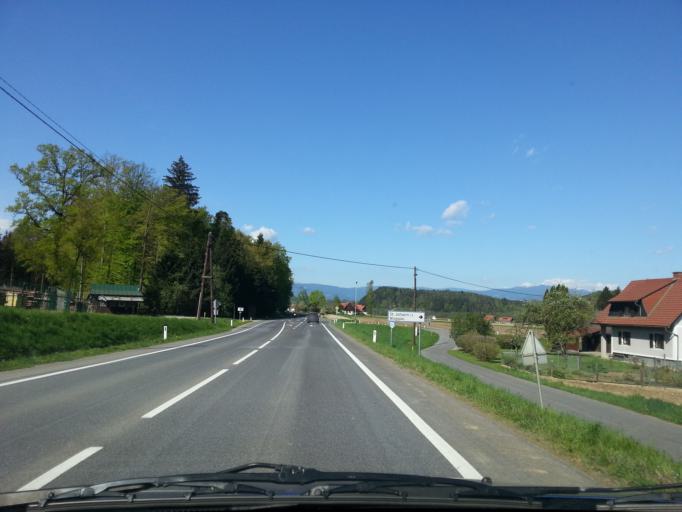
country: AT
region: Styria
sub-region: Politischer Bezirk Leibnitz
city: Arnfels
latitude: 46.6875
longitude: 15.3722
